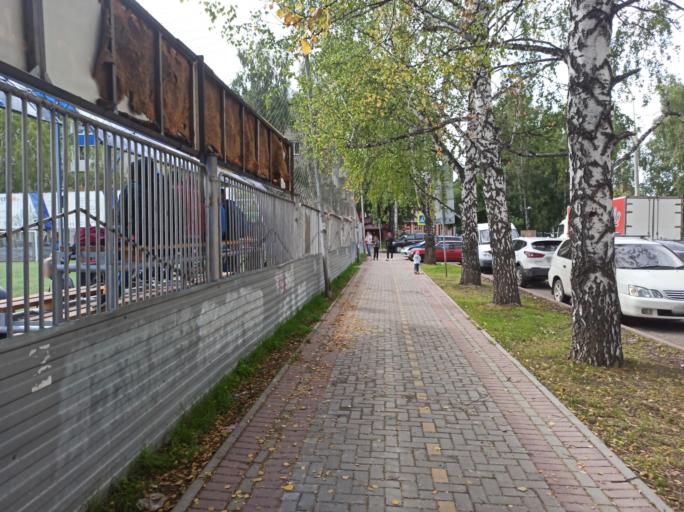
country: RU
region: Tomsk
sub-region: Tomskiy Rayon
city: Tomsk
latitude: 56.4624
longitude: 84.9850
